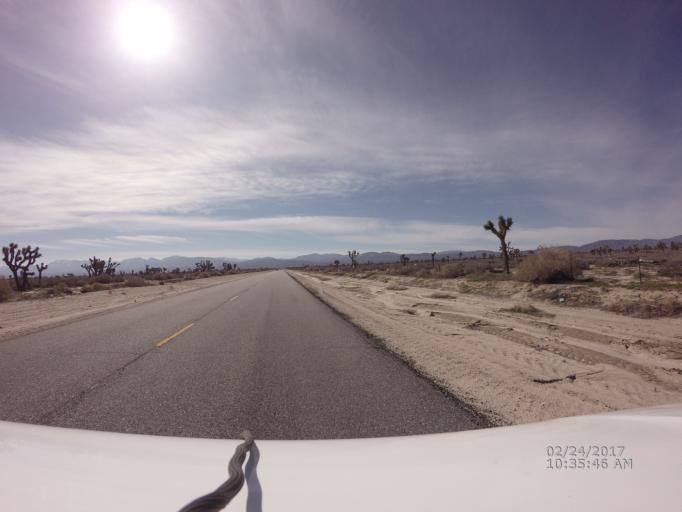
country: US
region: California
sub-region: Los Angeles County
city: Littlerock
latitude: 34.6002
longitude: -118.0051
